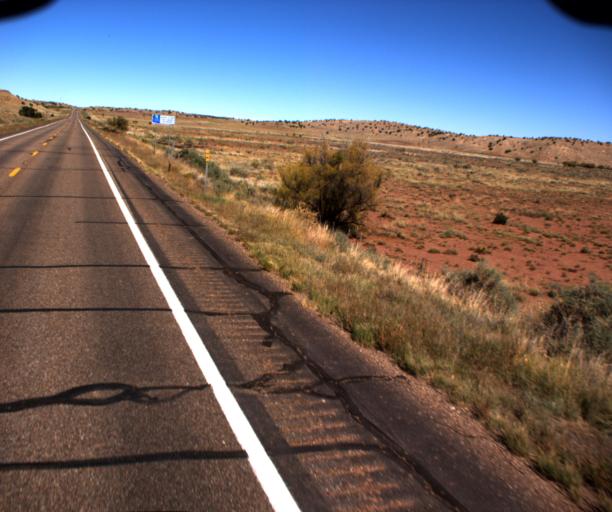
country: US
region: Arizona
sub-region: Apache County
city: Saint Johns
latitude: 34.3899
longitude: -109.4073
